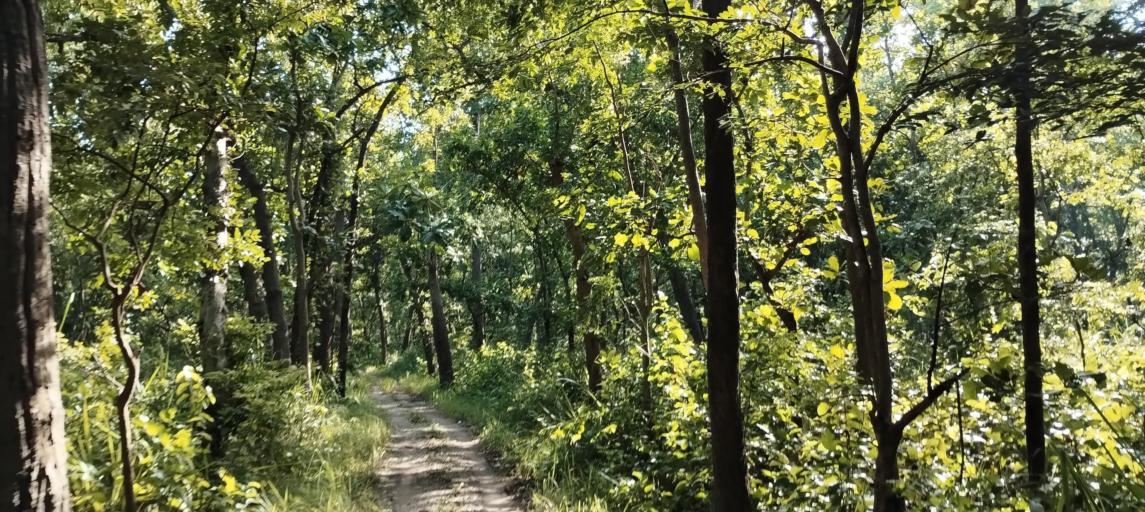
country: NP
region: Far Western
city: Tikapur
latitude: 28.5364
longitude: 81.2839
